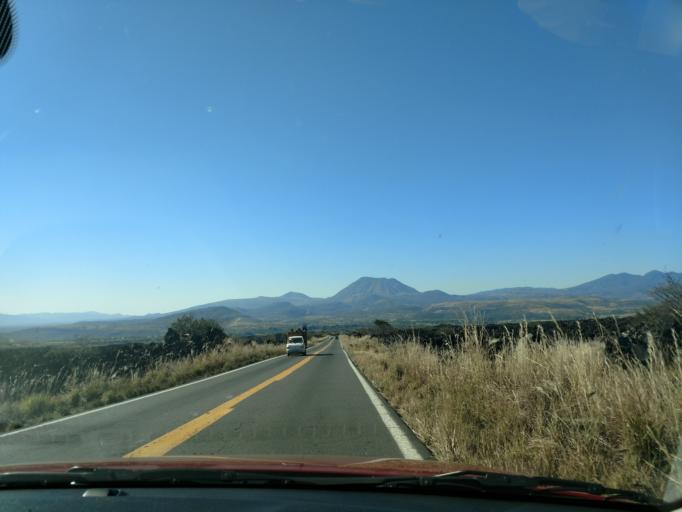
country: MX
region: Nayarit
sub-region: Ahuacatlan
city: Ahuacatlan
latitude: 21.0923
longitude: -104.5746
